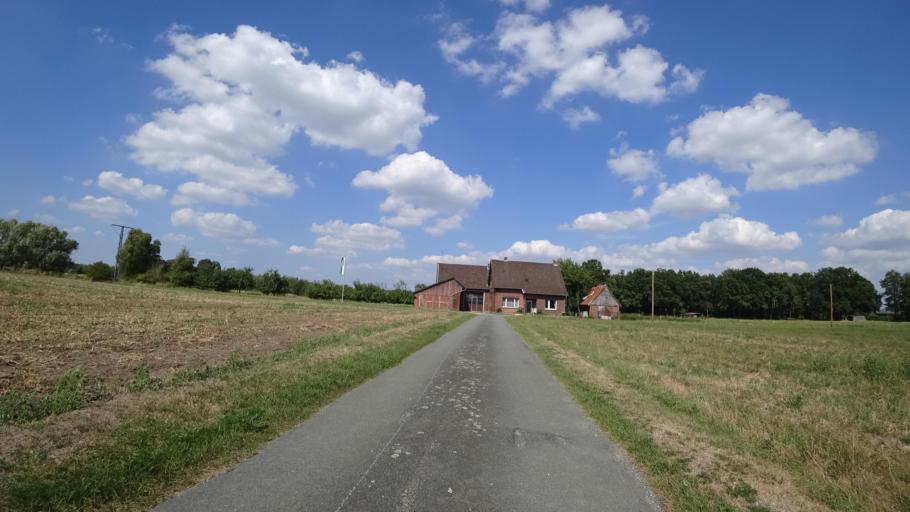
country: DE
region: North Rhine-Westphalia
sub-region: Regierungsbezirk Detmold
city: Rheda-Wiedenbruck
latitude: 51.8704
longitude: 8.2708
